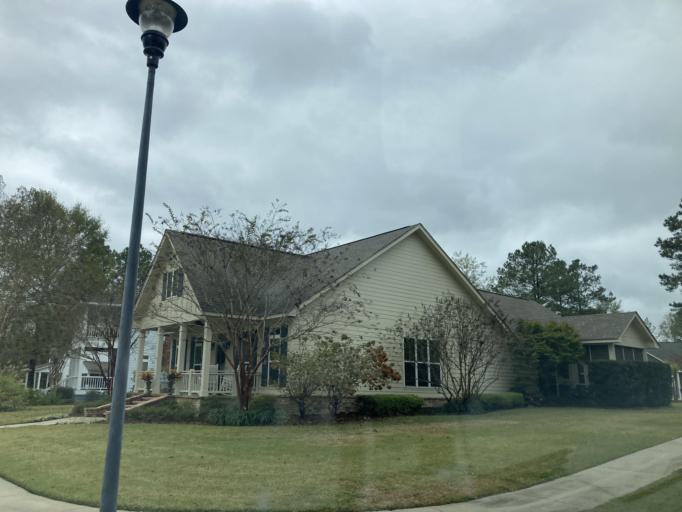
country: US
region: Mississippi
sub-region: Lamar County
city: West Hattiesburg
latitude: 31.2876
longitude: -89.4764
